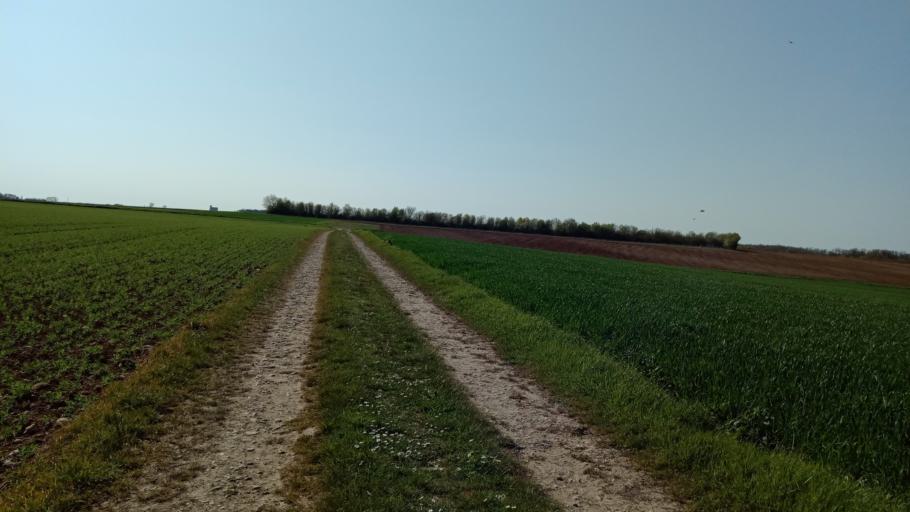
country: FR
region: Poitou-Charentes
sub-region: Departement de la Charente-Maritime
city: Verines
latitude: 46.1579
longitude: -0.9326
